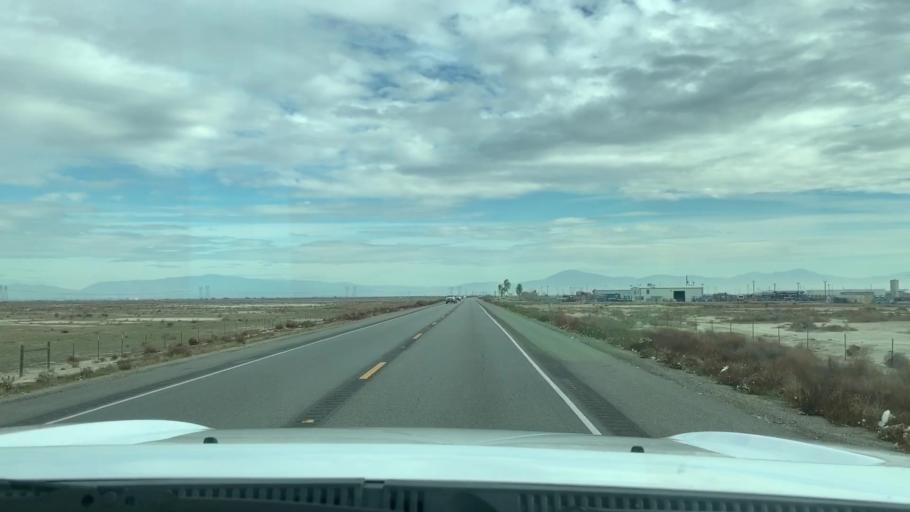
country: US
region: California
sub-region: Kern County
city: Rosedale
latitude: 35.2674
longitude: -119.2679
